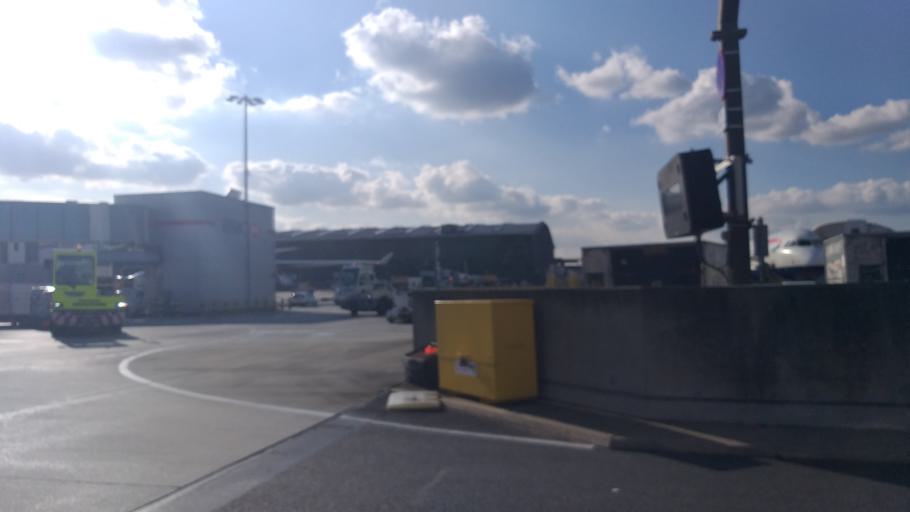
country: GB
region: England
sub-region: Greater London
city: West Drayton
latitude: 51.4737
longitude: -0.4813
